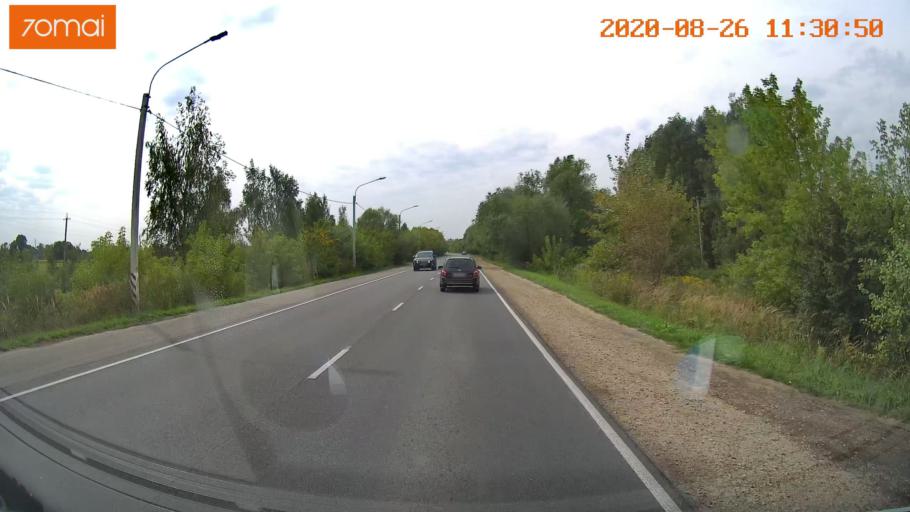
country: RU
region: Rjazan
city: Shilovo
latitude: 54.3122
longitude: 40.8785
